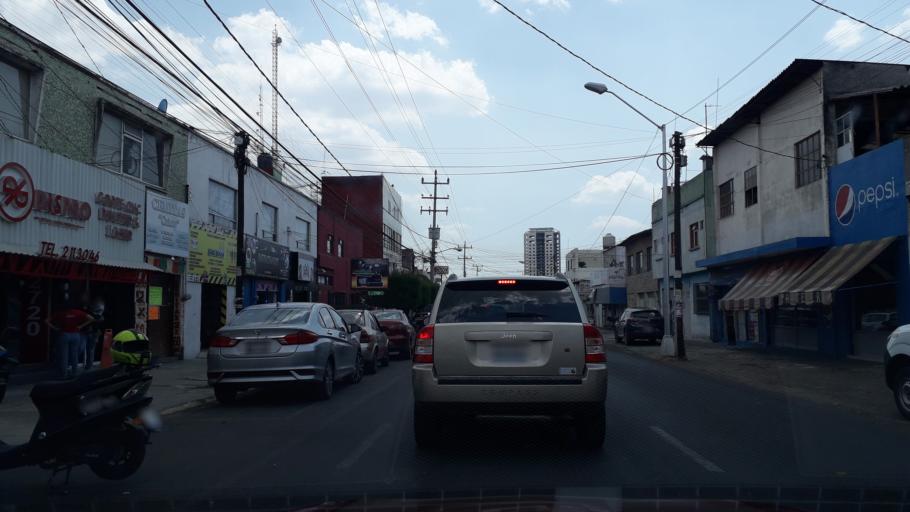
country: MX
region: Puebla
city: Puebla
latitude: 19.0404
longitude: -98.2181
